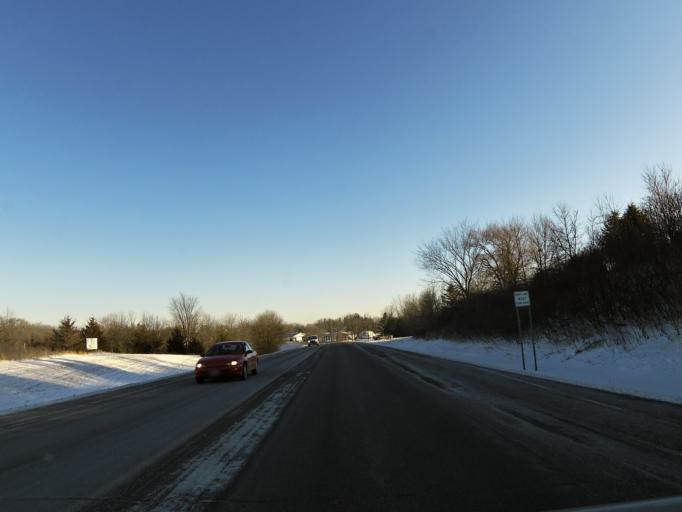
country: US
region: Minnesota
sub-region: Rice County
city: Lonsdale
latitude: 44.4832
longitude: -93.4383
